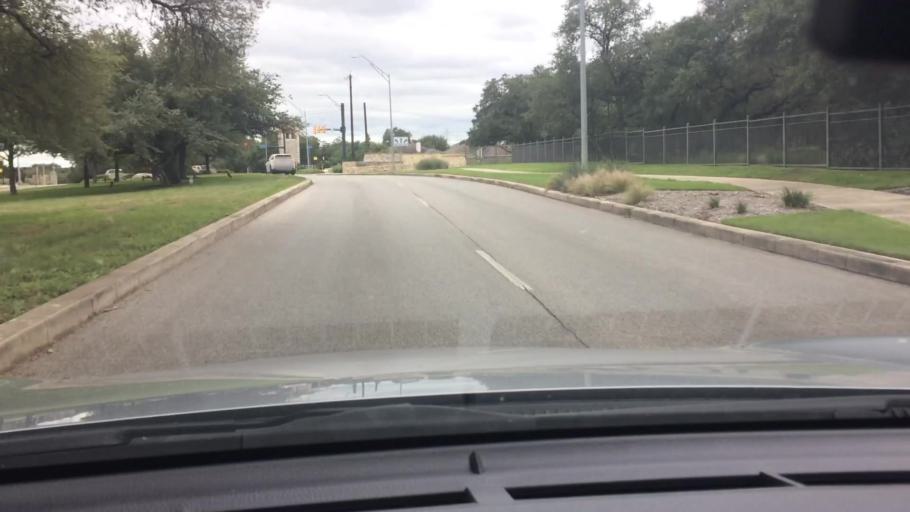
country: US
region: Texas
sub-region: Bexar County
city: Timberwood Park
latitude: 29.6465
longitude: -98.4019
